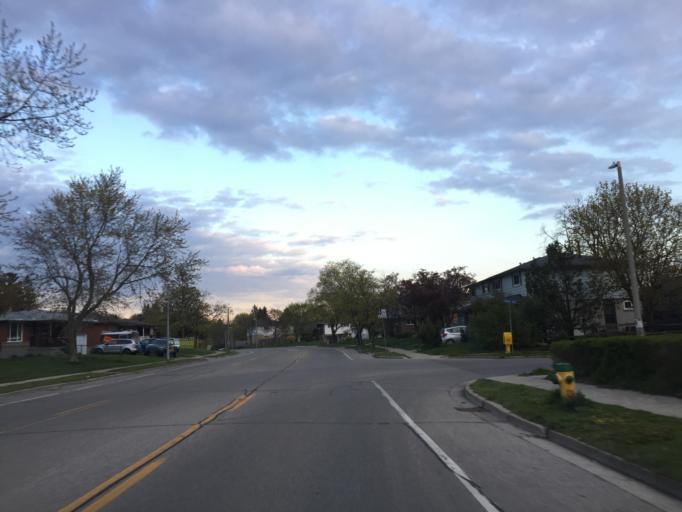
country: CA
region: Ontario
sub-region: Wellington County
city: Guelph
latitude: 43.5116
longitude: -80.2529
